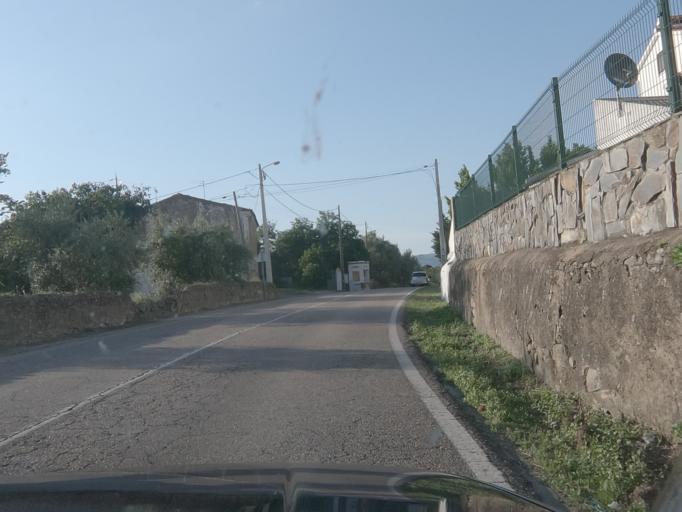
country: PT
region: Portalegre
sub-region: Portalegre
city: Portalegre
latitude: 39.3120
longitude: -7.4413
